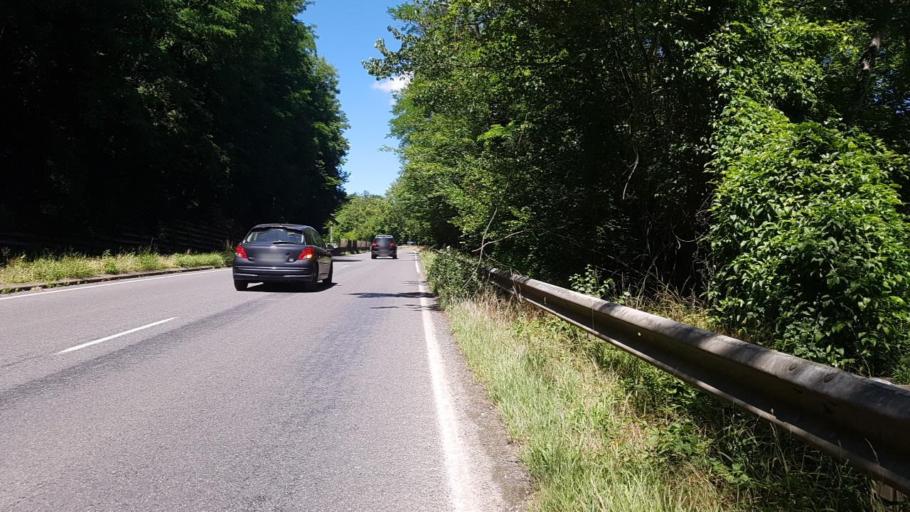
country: FR
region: Ile-de-France
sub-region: Departement de Seine-et-Marne
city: Saint-Jean-les-Deux-Jumeaux
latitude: 48.9578
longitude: 3.0033
